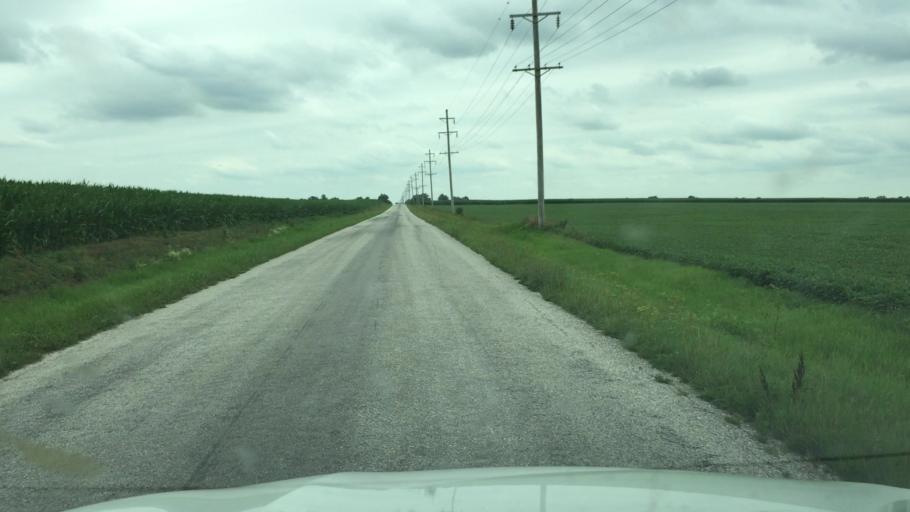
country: US
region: Illinois
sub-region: Hancock County
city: Carthage
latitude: 40.3412
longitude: -91.0823
